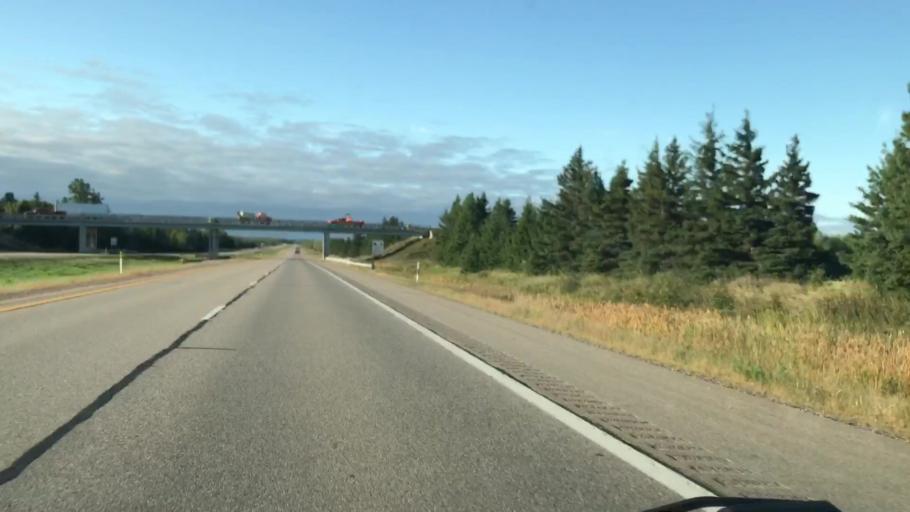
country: US
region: Michigan
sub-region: Chippewa County
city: Sault Ste. Marie
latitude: 46.4209
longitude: -84.3948
